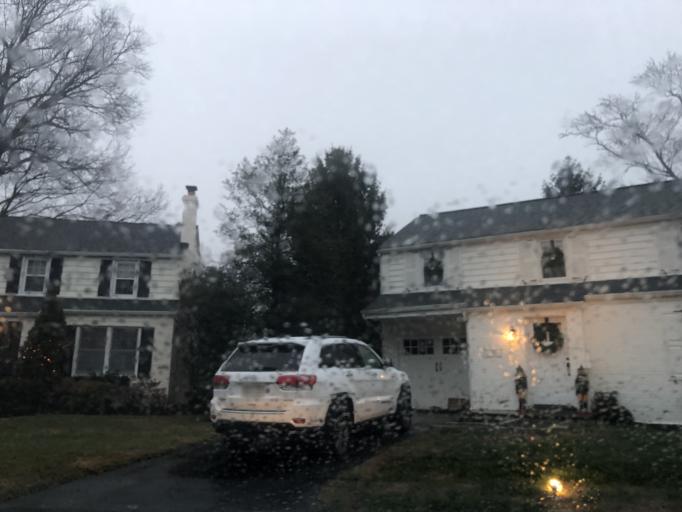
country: US
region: Pennsylvania
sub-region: Delaware County
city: Radnor
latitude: 40.0286
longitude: -75.3416
